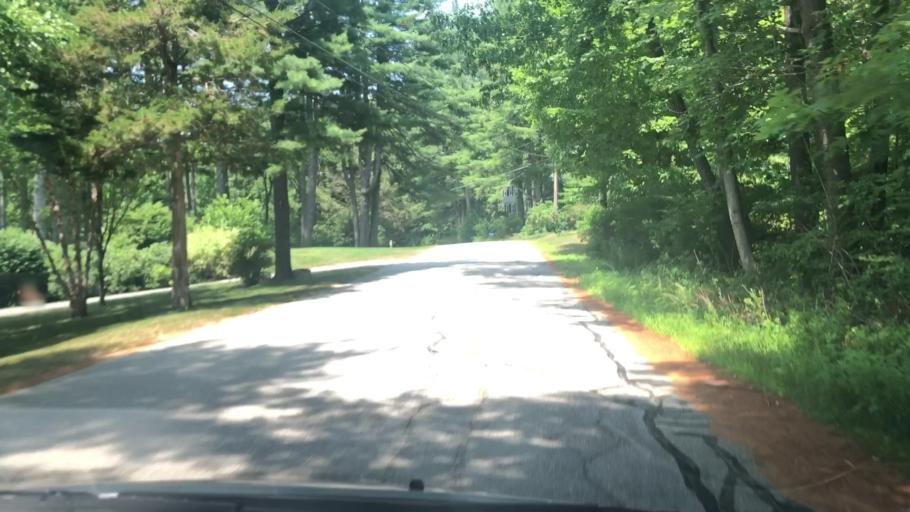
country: US
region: New Hampshire
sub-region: Hillsborough County
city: Milford
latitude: 42.8705
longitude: -71.6210
